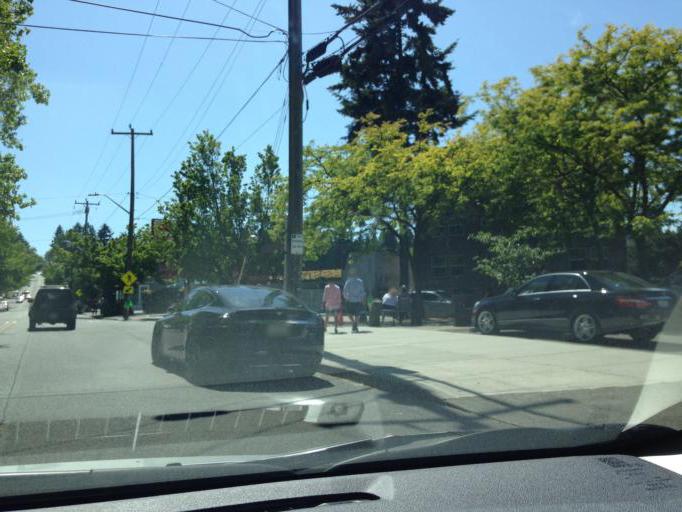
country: US
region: Washington
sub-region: King County
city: Medina
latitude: 47.6358
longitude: -122.2783
